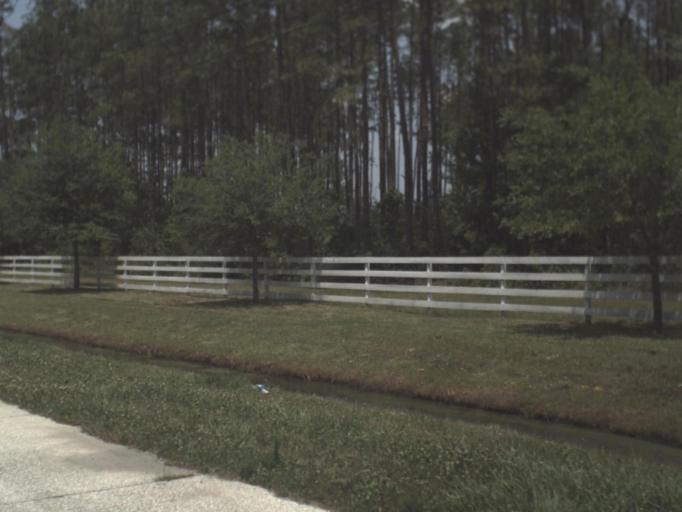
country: US
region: Florida
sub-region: Duval County
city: Baldwin
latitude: 30.2047
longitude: -81.9878
